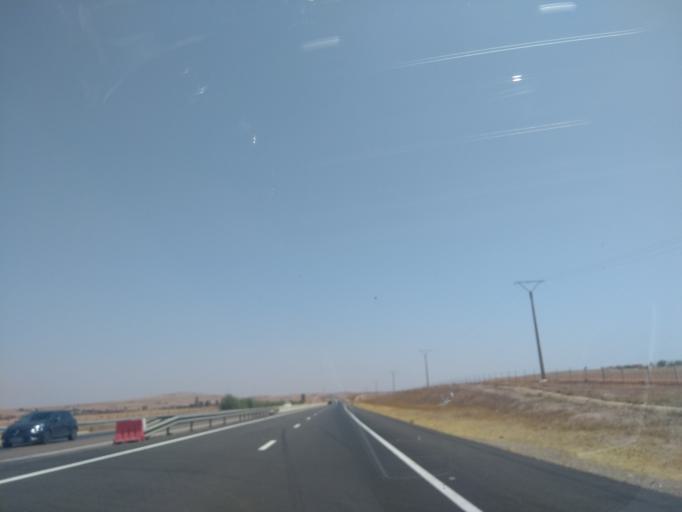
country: MA
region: Marrakech-Tensift-Al Haouz
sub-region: Kelaa-Des-Sraghna
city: Sidi Abdallah
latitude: 32.2860
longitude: -7.9652
